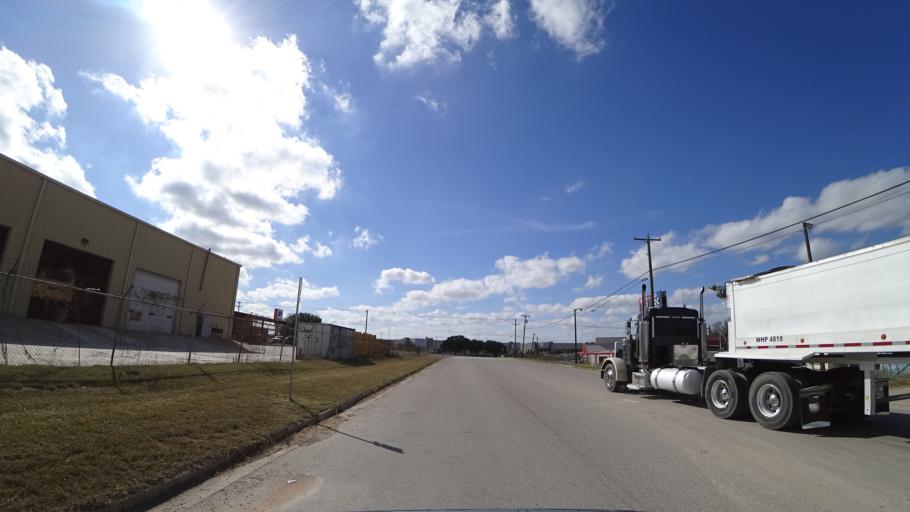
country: US
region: Texas
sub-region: Travis County
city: Windemere
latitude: 30.4604
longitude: -97.6655
